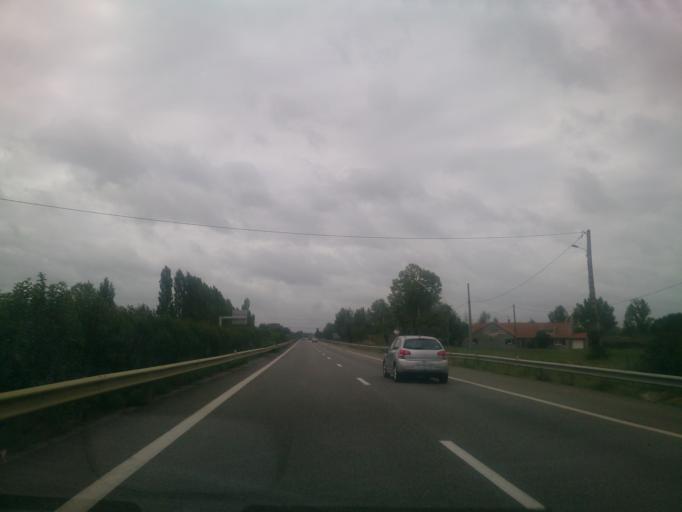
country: FR
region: Midi-Pyrenees
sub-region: Departement de la Haute-Garonne
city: Le Fauga
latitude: 43.3819
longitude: 1.2812
